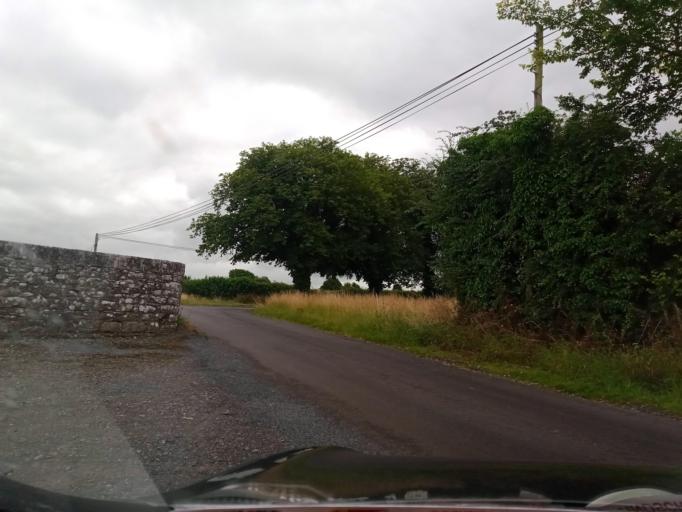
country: IE
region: Leinster
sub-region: Laois
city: Stradbally
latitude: 52.9915
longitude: -7.1745
